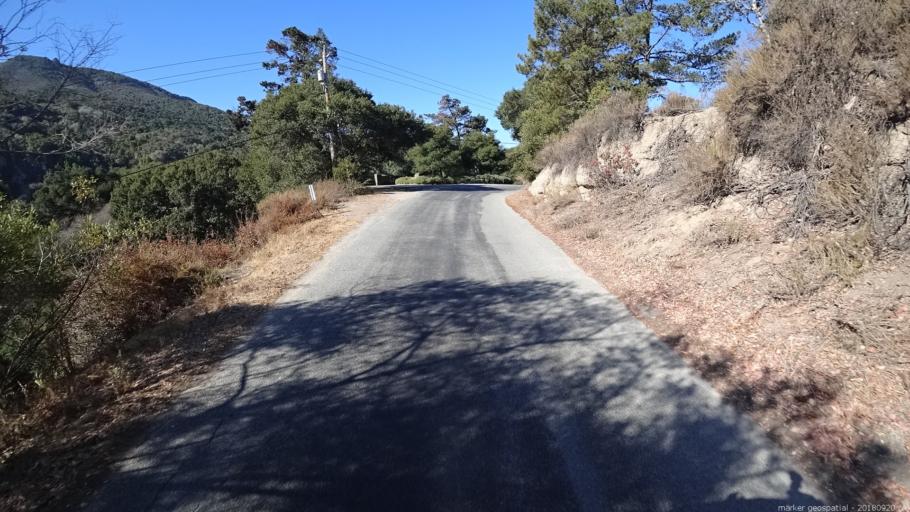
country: US
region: California
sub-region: Monterey County
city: Carmel Valley Village
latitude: 36.5185
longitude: -121.7884
